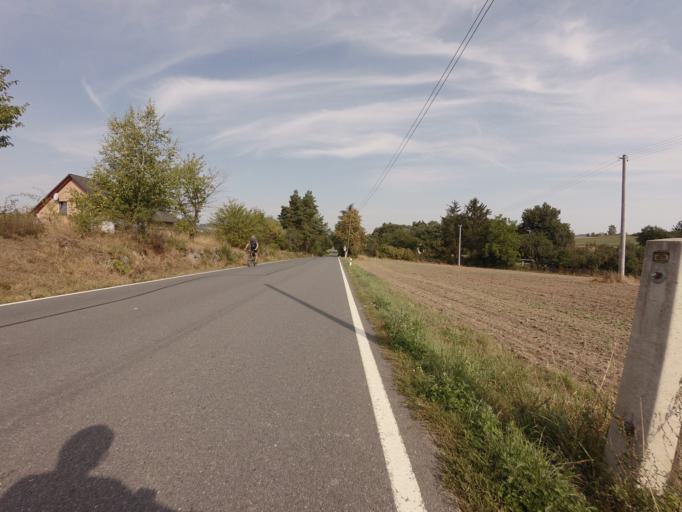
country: CZ
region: Central Bohemia
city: Petrovice
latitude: 49.5452
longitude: 14.3469
